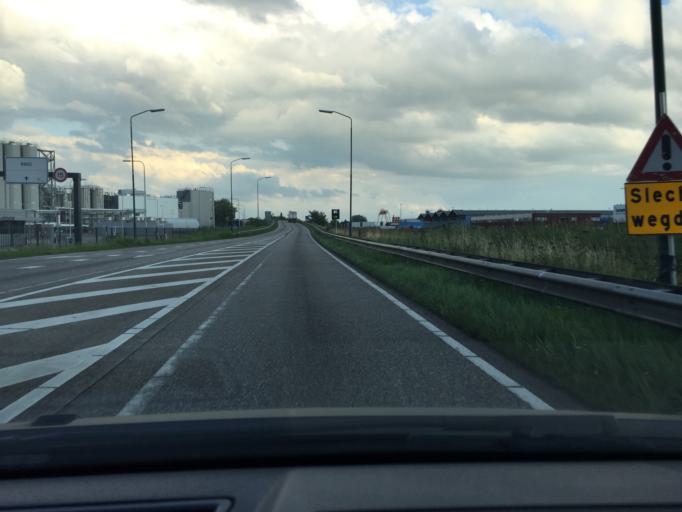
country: NL
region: North Brabant
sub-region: Gemeente Veghel
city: Eerde
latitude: 51.6157
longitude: 5.5190
